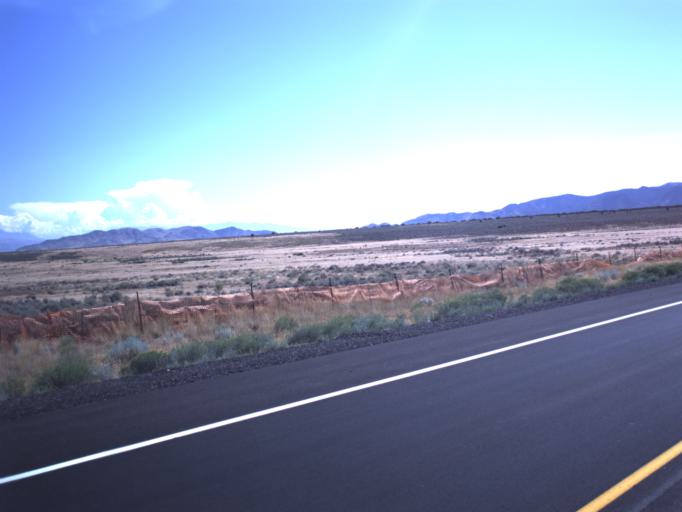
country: US
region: Utah
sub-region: Utah County
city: Eagle Mountain
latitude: 40.0751
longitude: -112.3406
